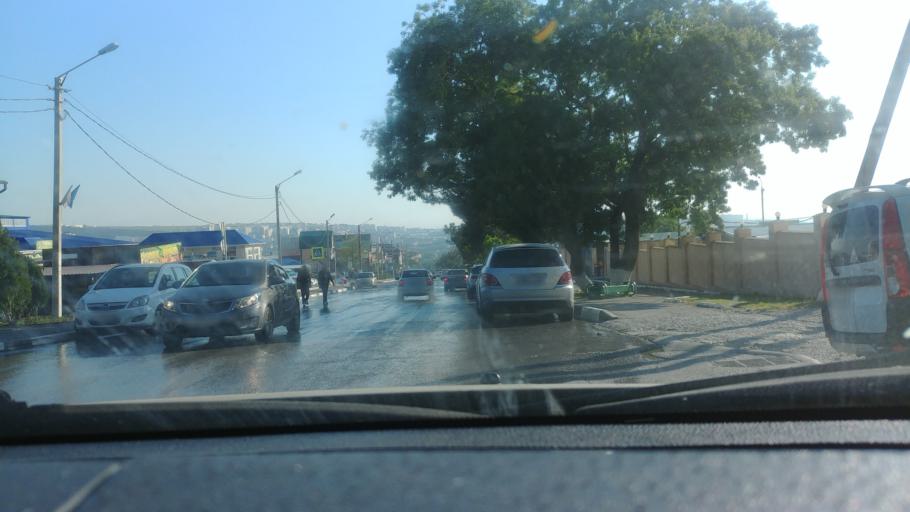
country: RU
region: Krasnodarskiy
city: Gelendzhik
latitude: 44.5709
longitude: 38.0924
